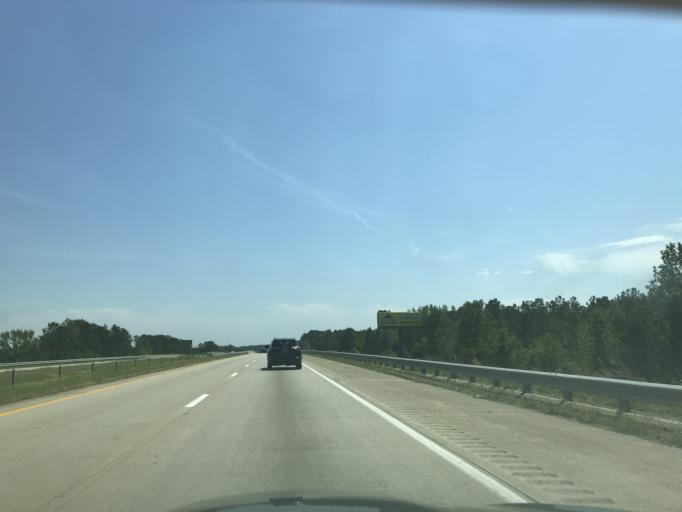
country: US
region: North Carolina
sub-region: Johnston County
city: Benson
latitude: 35.4068
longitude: -78.5240
